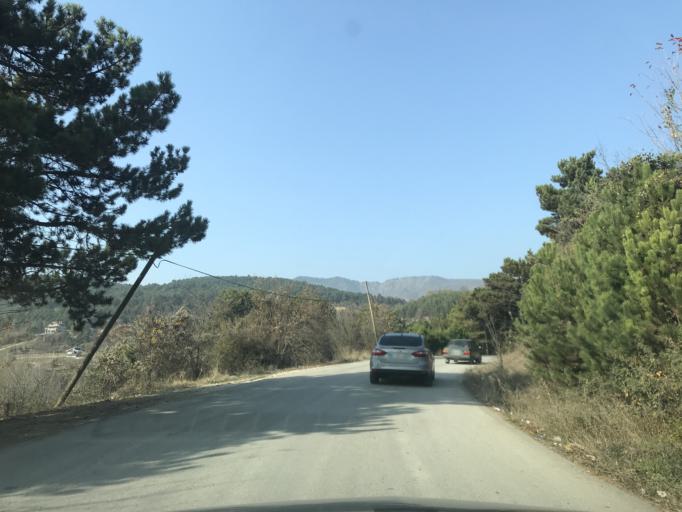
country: TR
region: Bolu
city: Bolu
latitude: 40.7801
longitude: 31.6323
